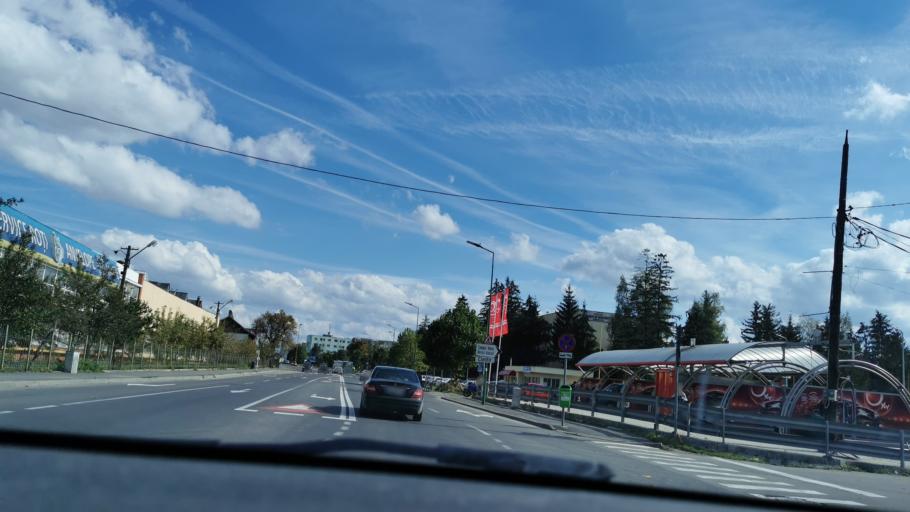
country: RO
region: Brasov
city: Brasov
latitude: 45.6491
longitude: 25.6377
